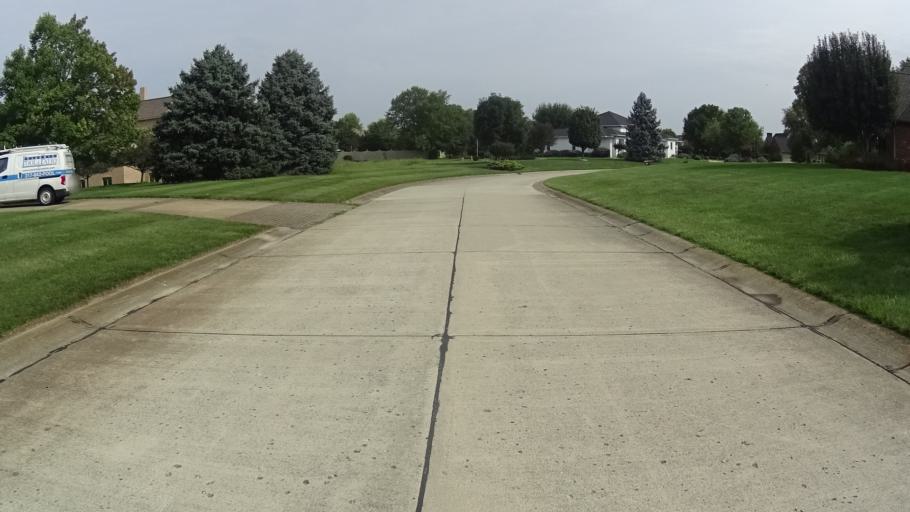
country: US
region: Indiana
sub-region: Madison County
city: Pendleton
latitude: 40.0123
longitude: -85.7878
